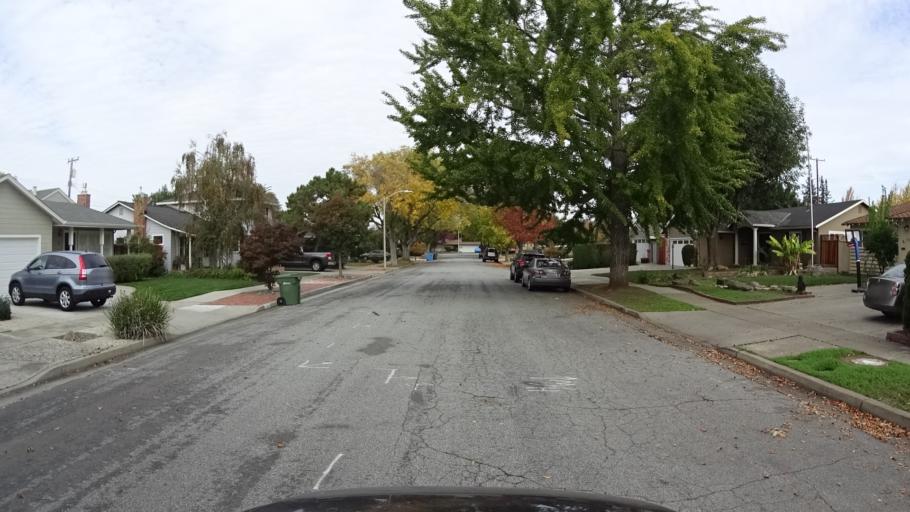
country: US
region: California
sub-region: Santa Clara County
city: Burbank
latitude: 37.3285
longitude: -121.9564
